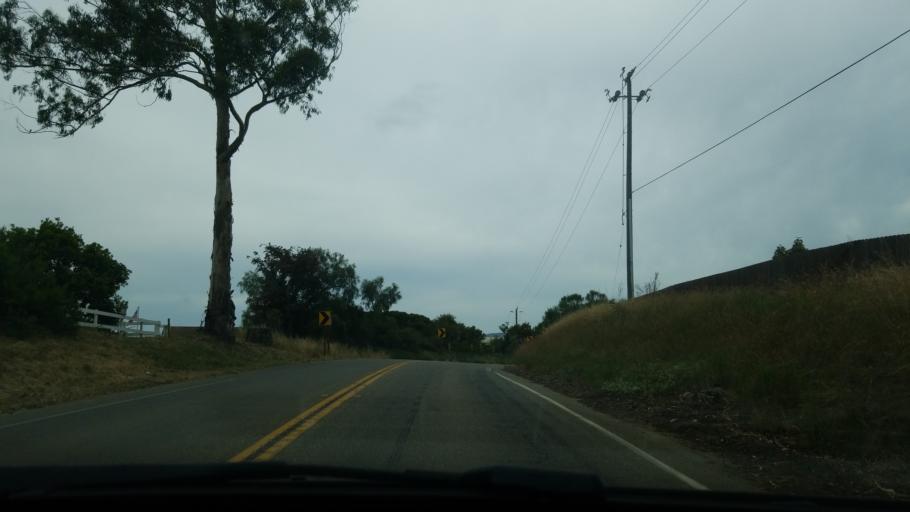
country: US
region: California
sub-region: San Luis Obispo County
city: Nipomo
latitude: 35.0095
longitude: -120.4952
